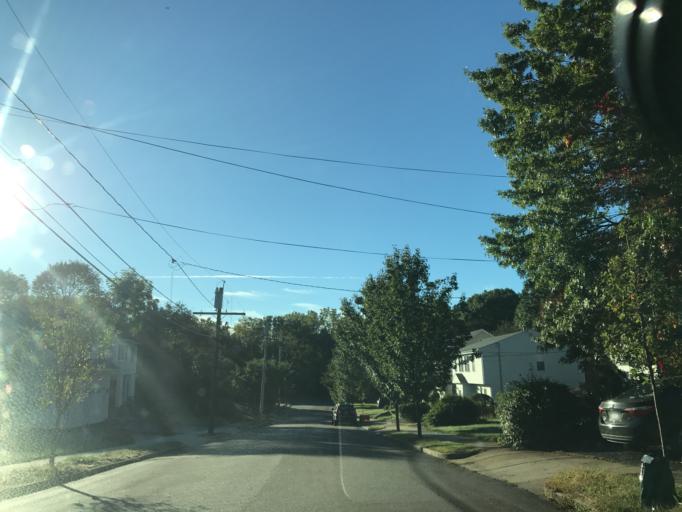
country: US
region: Massachusetts
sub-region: Norfolk County
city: Needham
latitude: 42.2911
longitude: -71.1921
